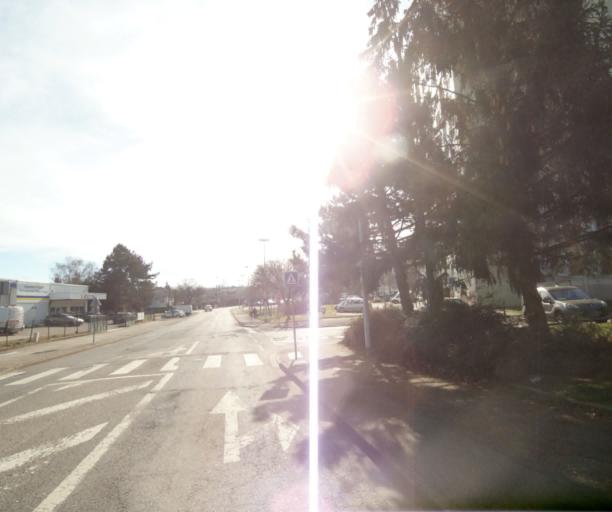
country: FR
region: Lorraine
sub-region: Departement de Meurthe-et-Moselle
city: Vandoeuvre-les-Nancy
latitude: 48.6656
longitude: 6.1829
